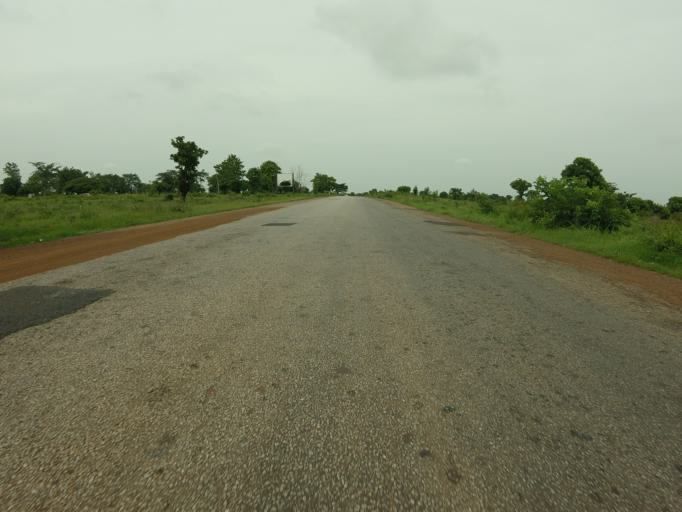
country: GH
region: Northern
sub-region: Yendi
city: Yendi
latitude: 9.4217
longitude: -0.0097
